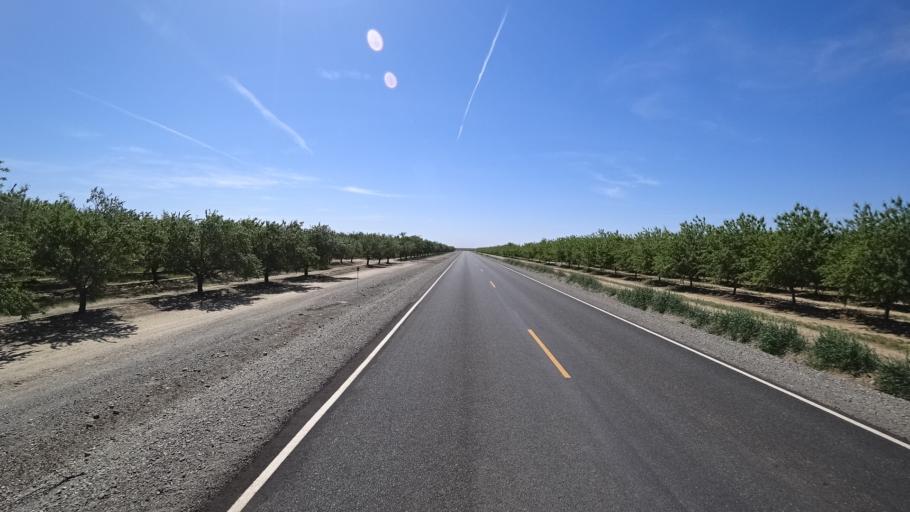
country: US
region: California
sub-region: Glenn County
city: Willows
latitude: 39.6280
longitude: -122.1414
